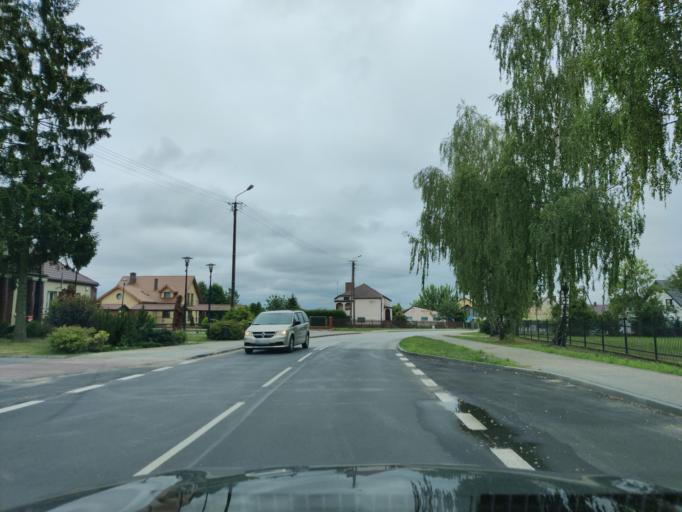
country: PL
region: Masovian Voivodeship
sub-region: Powiat makowski
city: Karniewo
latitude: 52.8360
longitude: 20.9895
